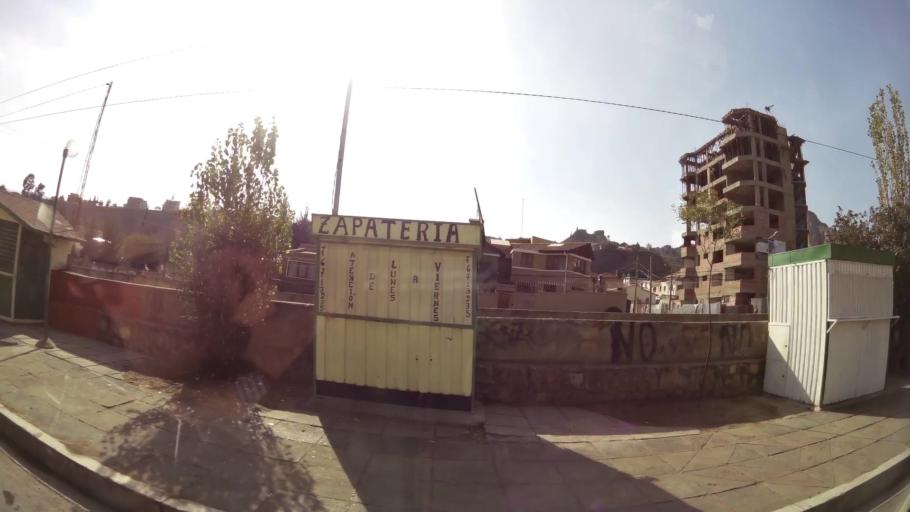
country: BO
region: La Paz
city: La Paz
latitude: -16.5287
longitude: -68.0719
